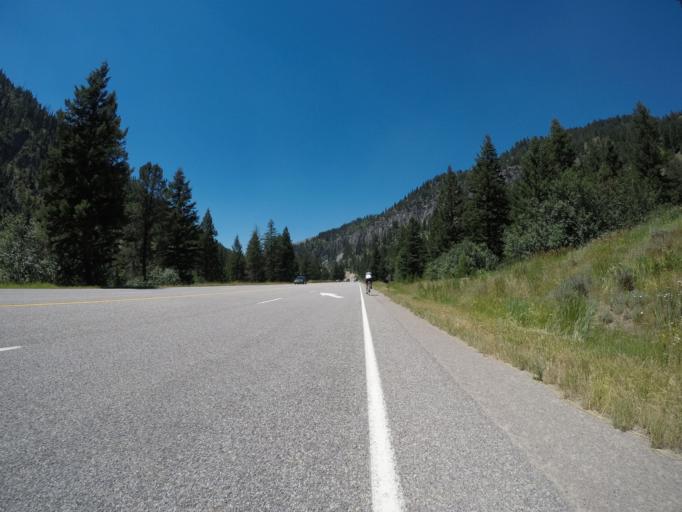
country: US
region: Wyoming
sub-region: Teton County
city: Hoback
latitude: 43.1981
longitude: -110.8987
